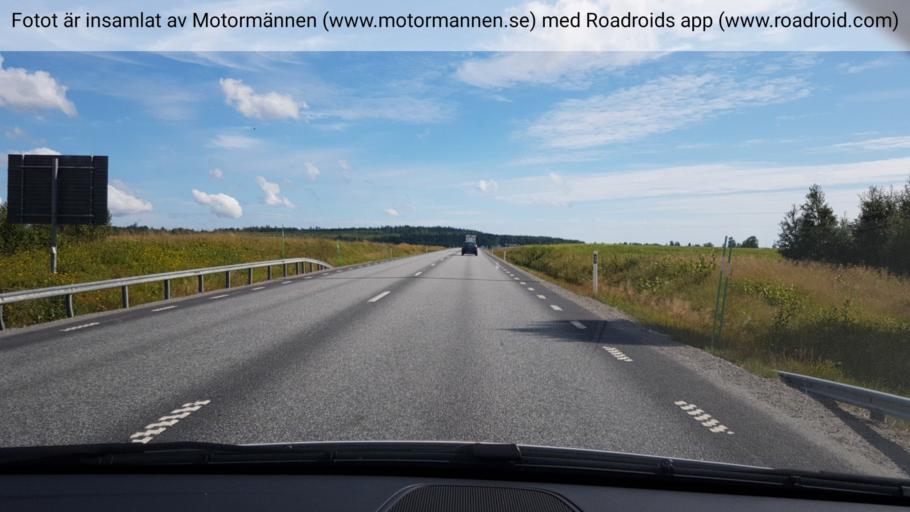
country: SE
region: Vaesterbotten
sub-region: Umea Kommun
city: Roback
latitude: 63.8728
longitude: 20.0677
